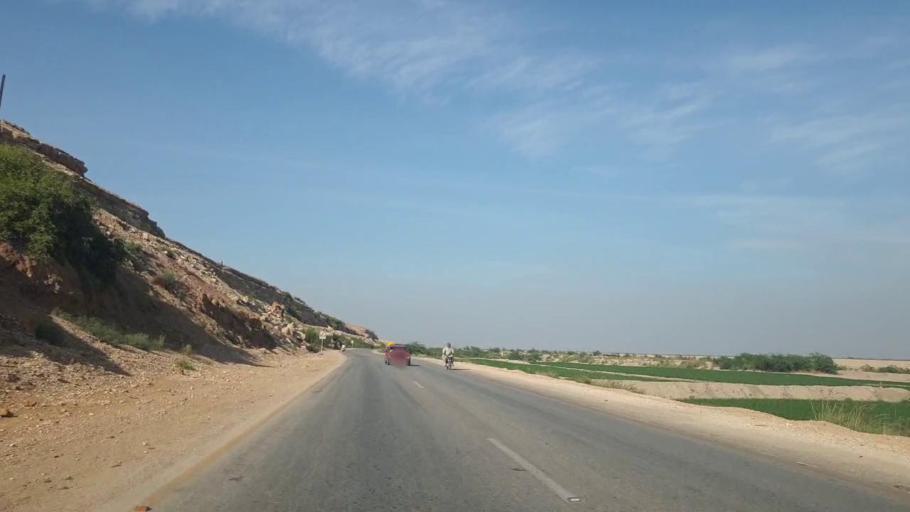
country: PK
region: Sindh
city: Sehwan
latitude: 26.3639
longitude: 67.8738
